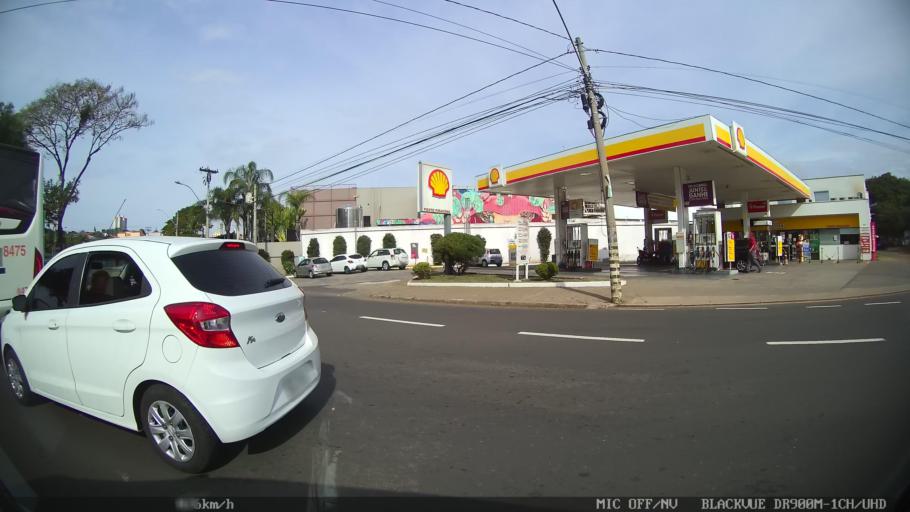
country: BR
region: Sao Paulo
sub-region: Piracicaba
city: Piracicaba
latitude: -22.7389
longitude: -47.6305
